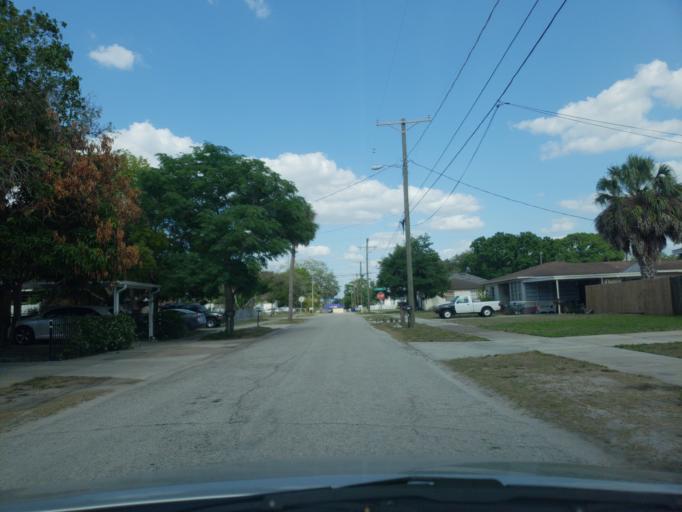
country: US
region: Florida
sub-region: Hillsborough County
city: Tampa
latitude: 27.9733
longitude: -82.4875
